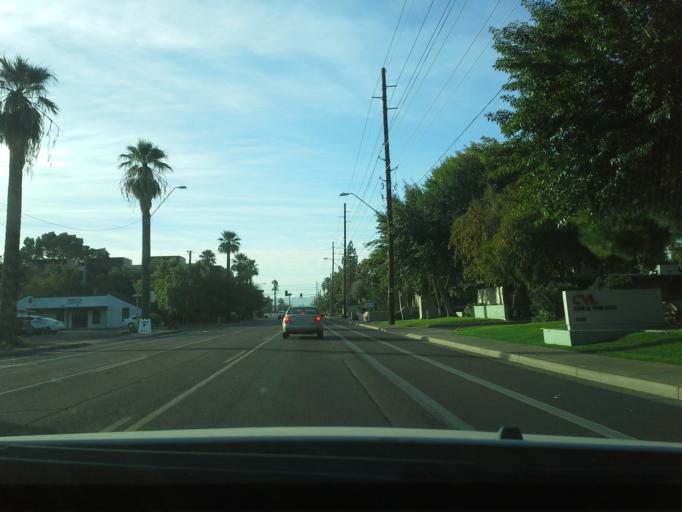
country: US
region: Arizona
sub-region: Maricopa County
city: Phoenix
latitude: 33.5036
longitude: -112.0564
